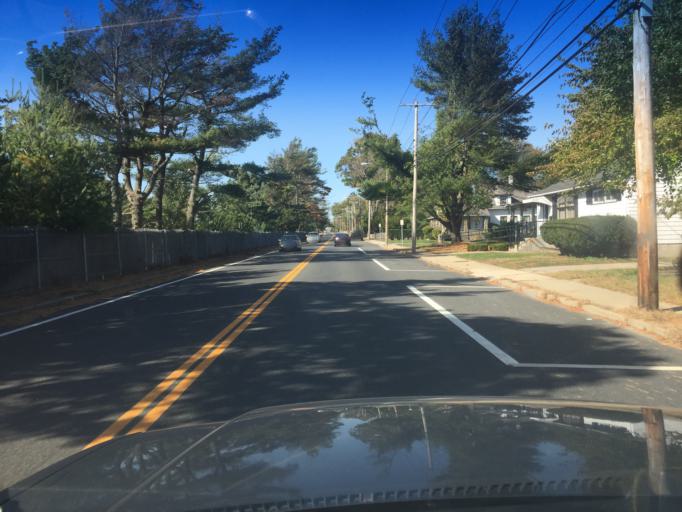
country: US
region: Rhode Island
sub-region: Providence County
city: Pawtucket
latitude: 41.8505
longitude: -71.3571
